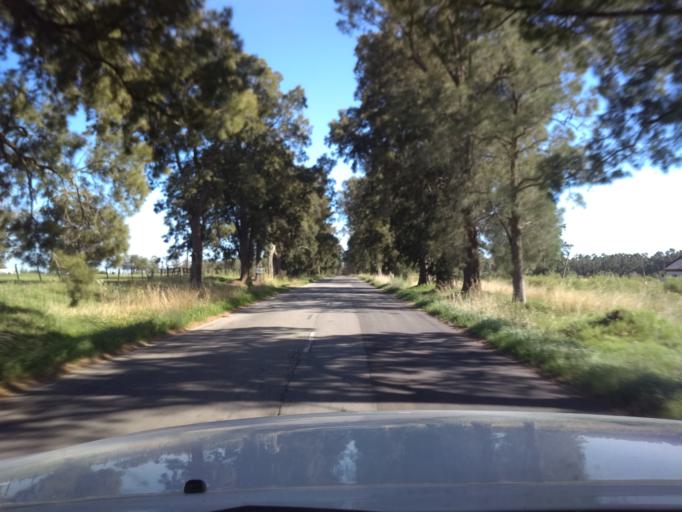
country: UY
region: Canelones
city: San Bautista
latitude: -34.3852
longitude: -55.9595
